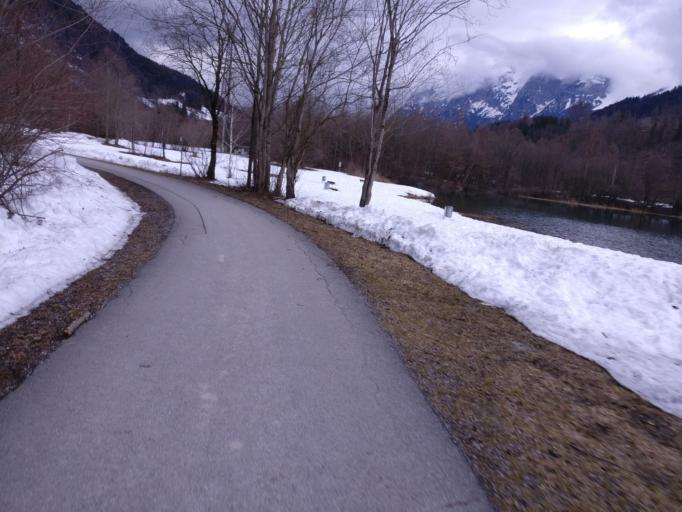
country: AT
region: Salzburg
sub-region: Politischer Bezirk Sankt Johann im Pongau
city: Bischofshofen
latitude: 47.4287
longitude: 13.2191
